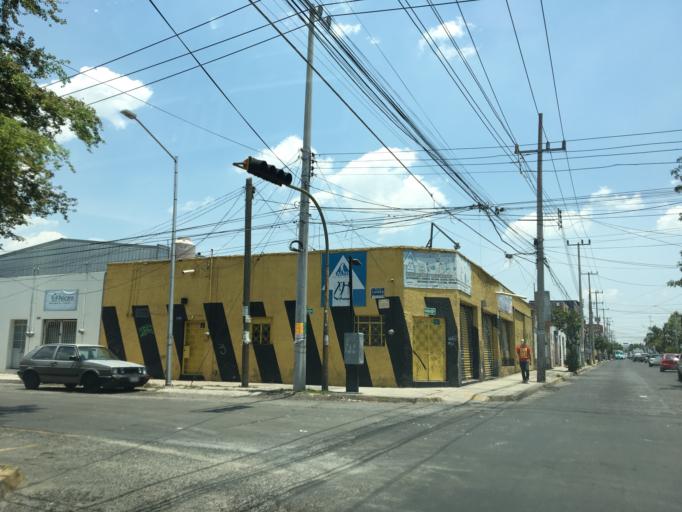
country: MX
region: Jalisco
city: Guadalajara
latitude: 20.6588
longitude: -103.3682
